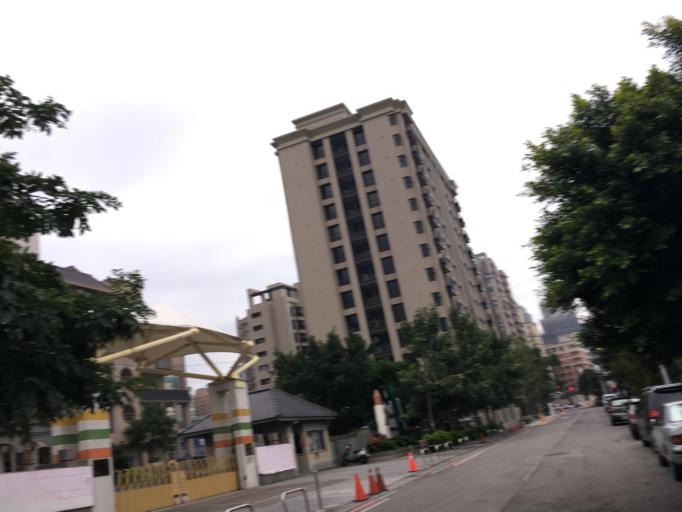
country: TW
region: Taiwan
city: Taoyuan City
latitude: 25.0185
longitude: 121.3066
